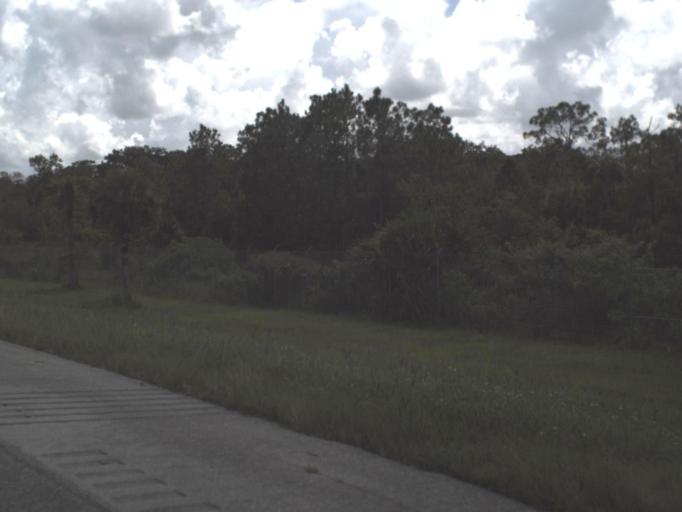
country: US
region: Florida
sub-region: Collier County
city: Orangetree
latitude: 26.1531
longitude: -81.4688
